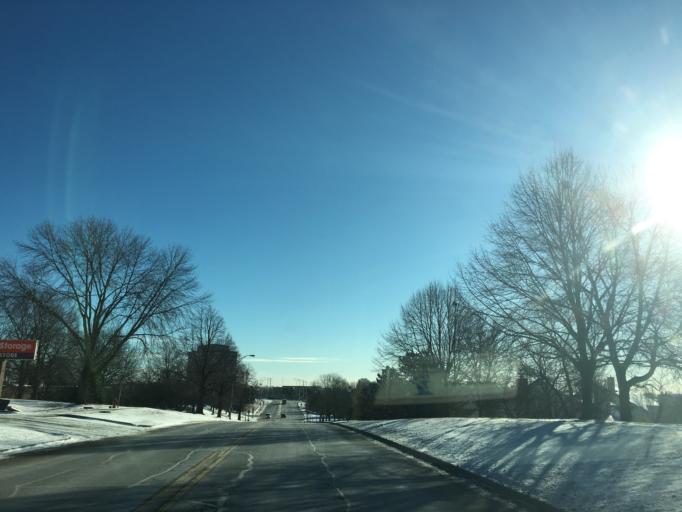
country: US
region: Illinois
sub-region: Cook County
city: Hoffman Estates
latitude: 42.0603
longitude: -88.0845
